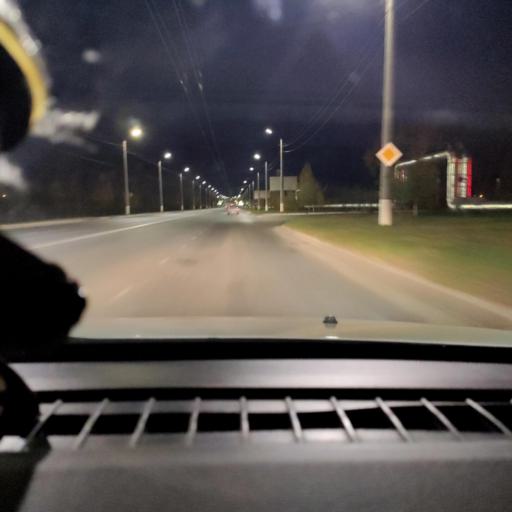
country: RU
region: Samara
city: Novokuybyshevsk
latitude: 53.1015
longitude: 49.9394
